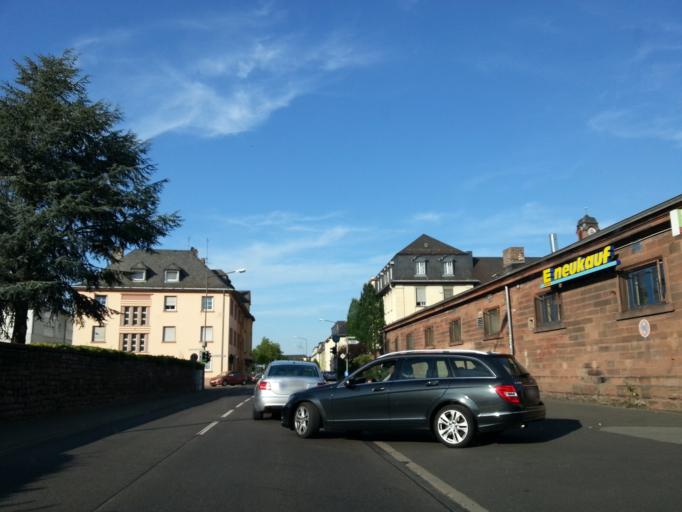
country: DE
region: Rheinland-Pfalz
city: Trier
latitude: 49.7615
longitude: 6.6540
